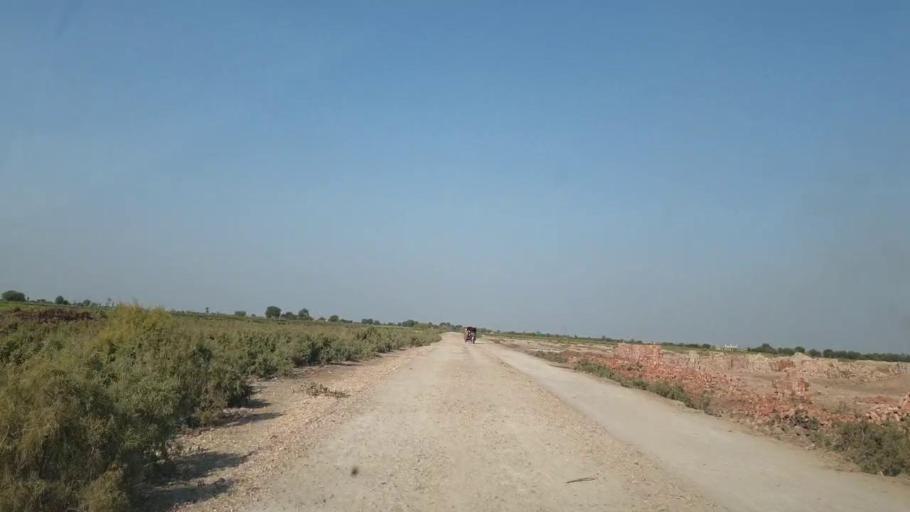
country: PK
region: Sindh
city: Tando Mittha Khan
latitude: 25.7398
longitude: 69.1923
